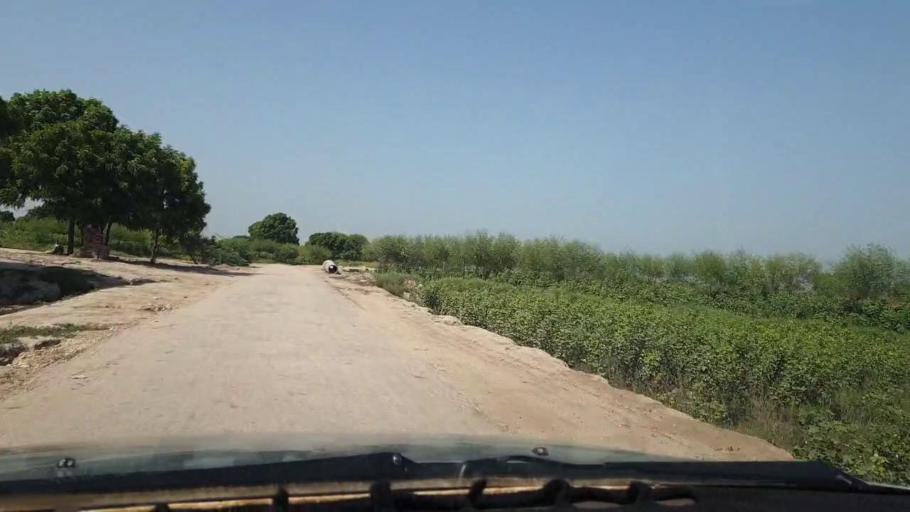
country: PK
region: Sindh
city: Tando Ghulam Ali
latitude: 25.2215
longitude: 68.8703
